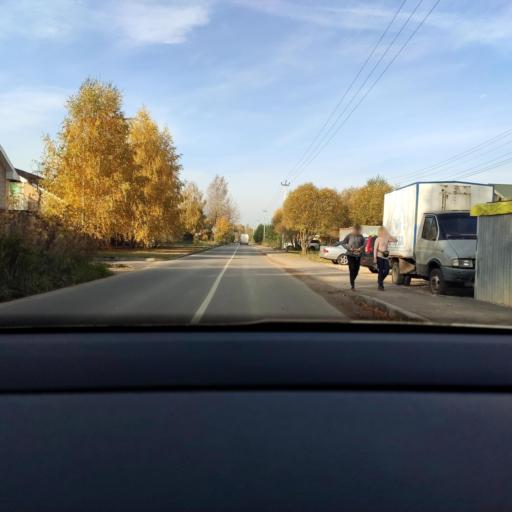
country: RU
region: Moskovskaya
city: Zagoryanskiy
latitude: 55.9648
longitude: 37.9638
